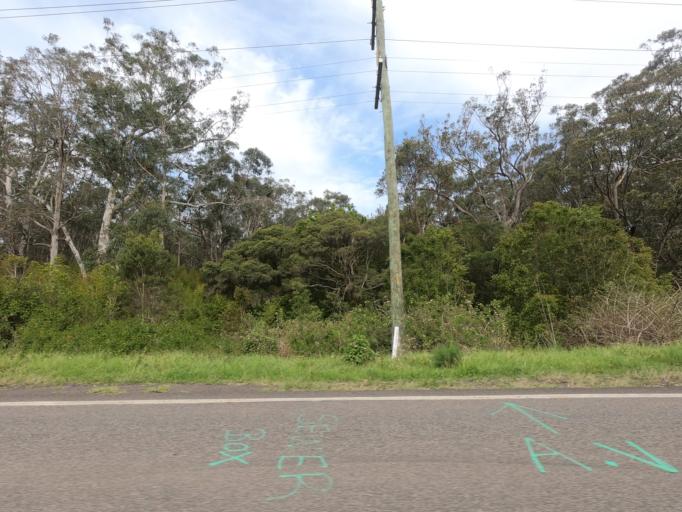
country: AU
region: New South Wales
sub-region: Wollongong
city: Dapto
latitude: -34.4740
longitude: 150.7909
